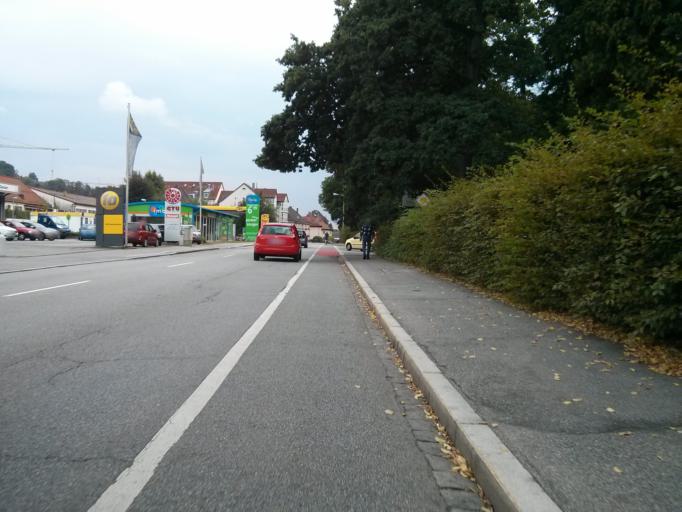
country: DE
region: Bavaria
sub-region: Lower Bavaria
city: Deggendorf
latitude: 48.8452
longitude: 12.9593
